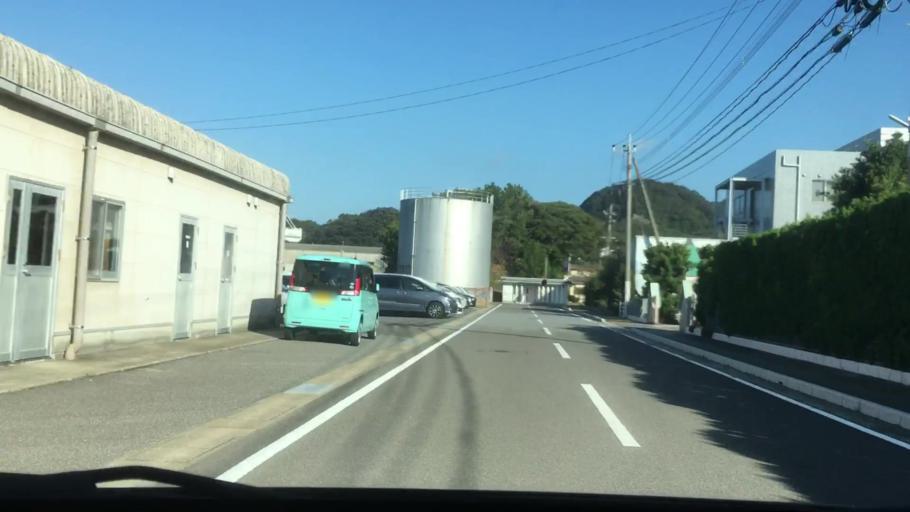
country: JP
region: Nagasaki
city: Sasebo
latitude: 32.9436
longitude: 129.6378
